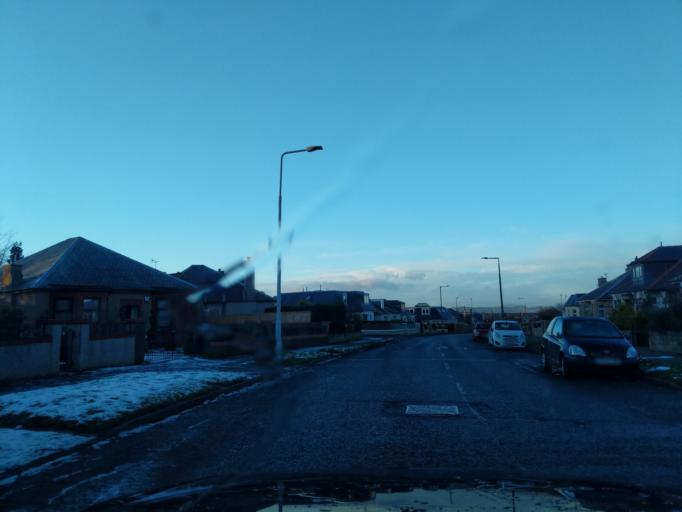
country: GB
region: Scotland
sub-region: West Lothian
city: Seafield
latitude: 55.9416
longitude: -3.1214
